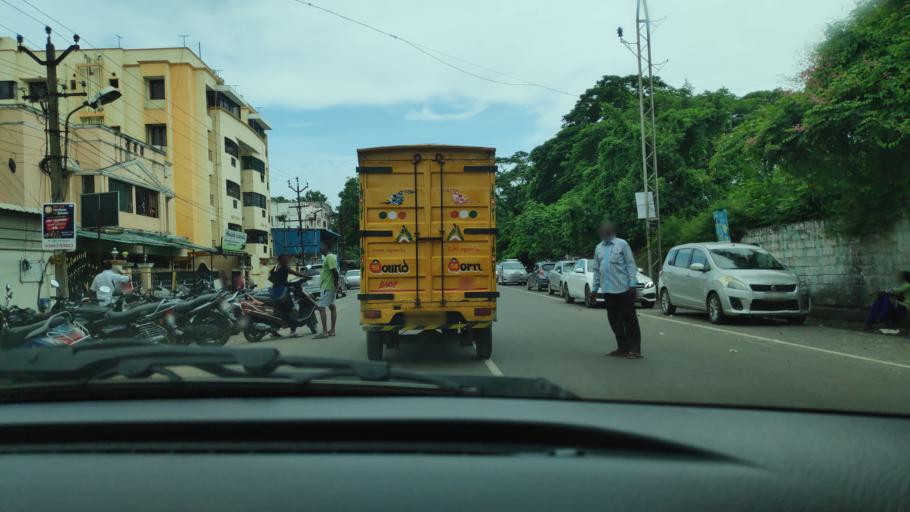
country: IN
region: Tamil Nadu
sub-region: Kancheepuram
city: Pallavaram
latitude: 12.9252
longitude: 80.1263
